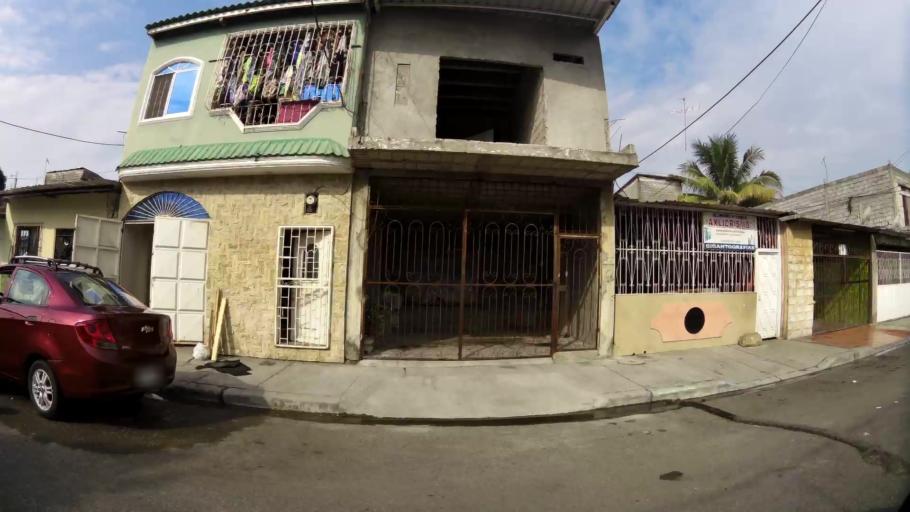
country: EC
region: Guayas
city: Guayaquil
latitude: -2.2469
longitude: -79.9049
